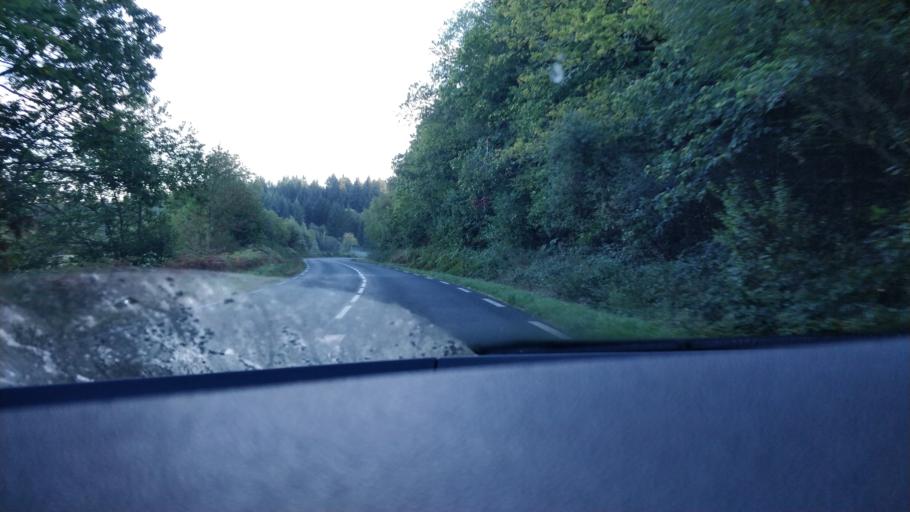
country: FR
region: Limousin
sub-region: Departement de la Haute-Vienne
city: Sauviat-sur-Vige
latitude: 45.9239
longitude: 1.6449
